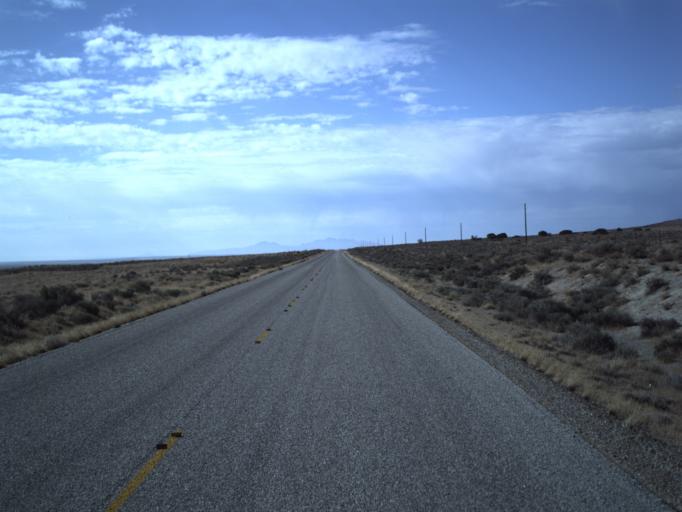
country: US
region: Utah
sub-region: Tooele County
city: Wendover
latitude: 41.5285
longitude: -113.5946
